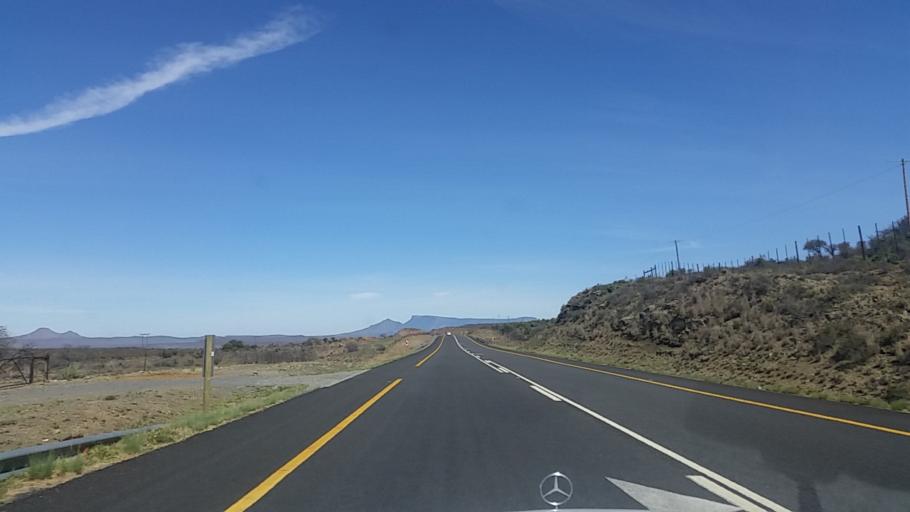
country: ZA
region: Eastern Cape
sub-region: Cacadu District Municipality
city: Graaff-Reinet
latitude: -32.2982
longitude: 24.5200
